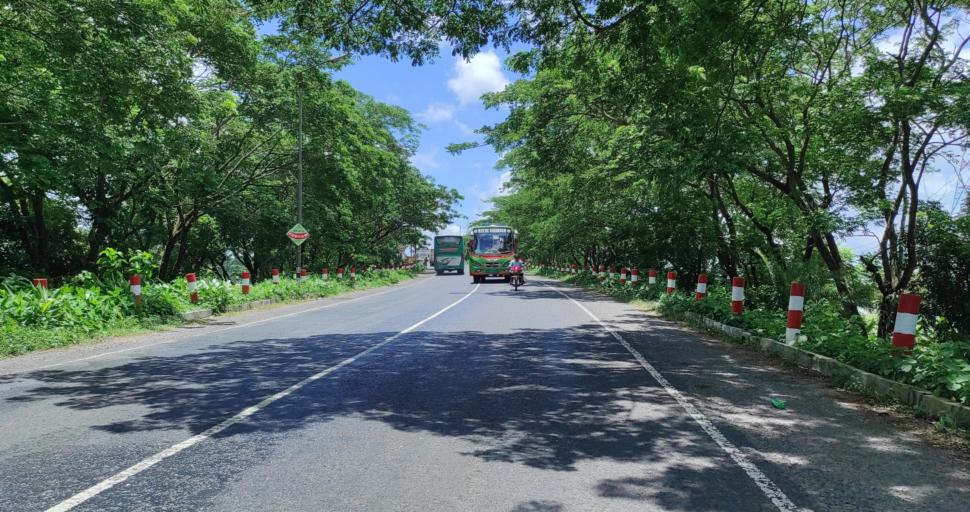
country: BD
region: Barisal
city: Gaurnadi
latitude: 22.8264
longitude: 90.2606
